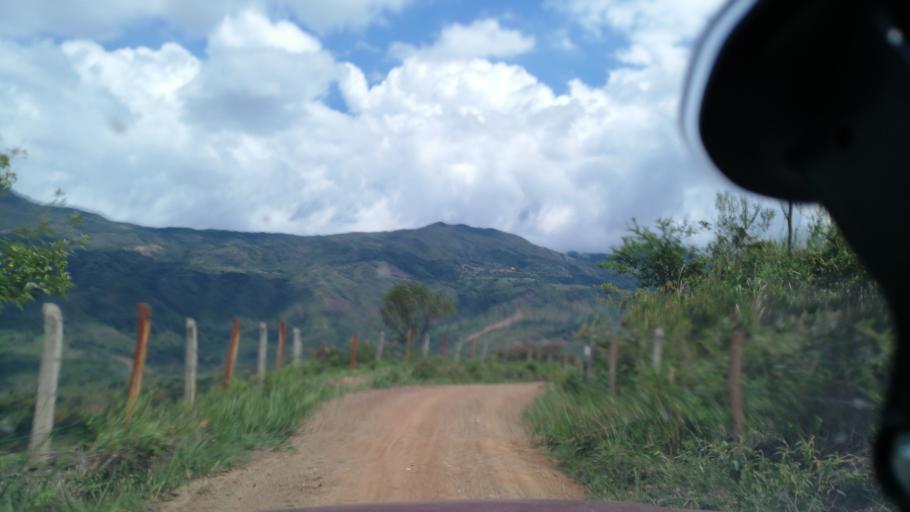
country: CO
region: Cundinamarca
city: Quipile
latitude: 4.7784
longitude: -74.6188
